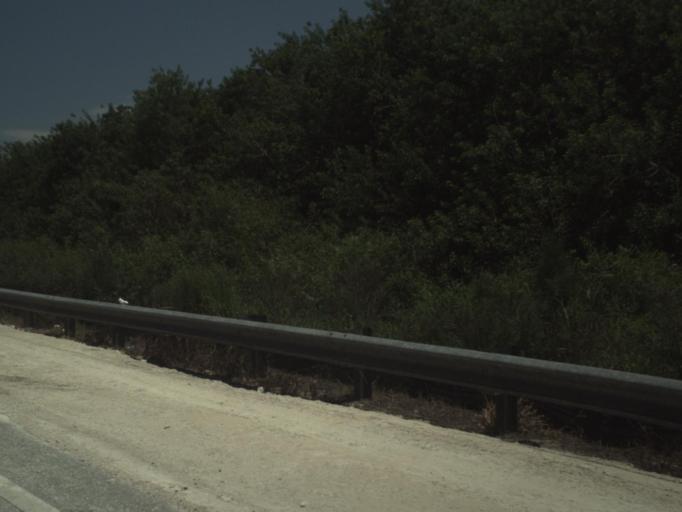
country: US
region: Florida
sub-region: Okeechobee County
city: Taylor Creek
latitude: 27.1383
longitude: -80.6461
